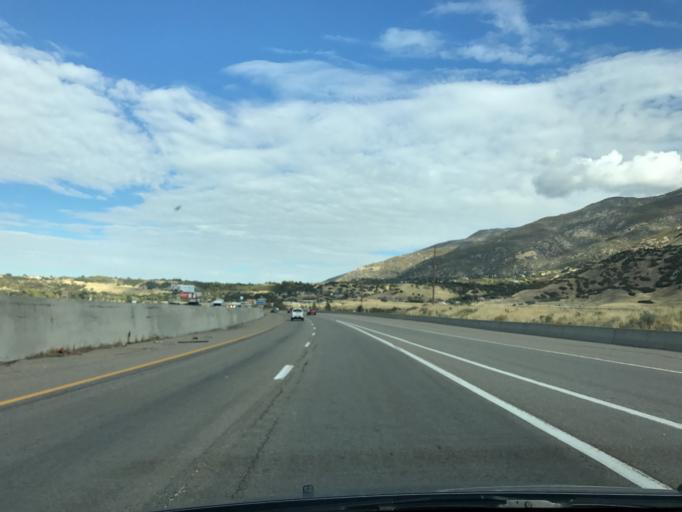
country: US
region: Utah
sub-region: Weber County
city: Uintah
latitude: 41.1284
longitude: -111.9081
